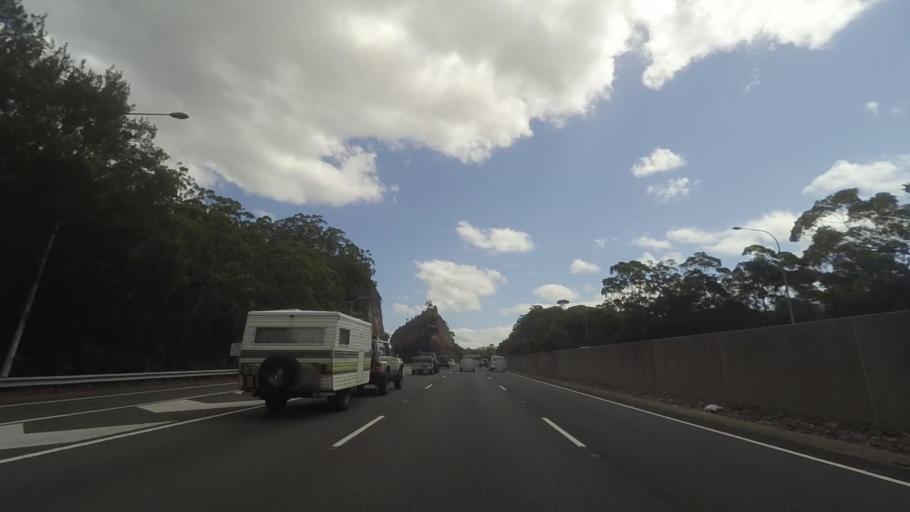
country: AU
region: New South Wales
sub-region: Hornsby Shire
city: Berowra
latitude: -33.6014
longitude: 151.1686
